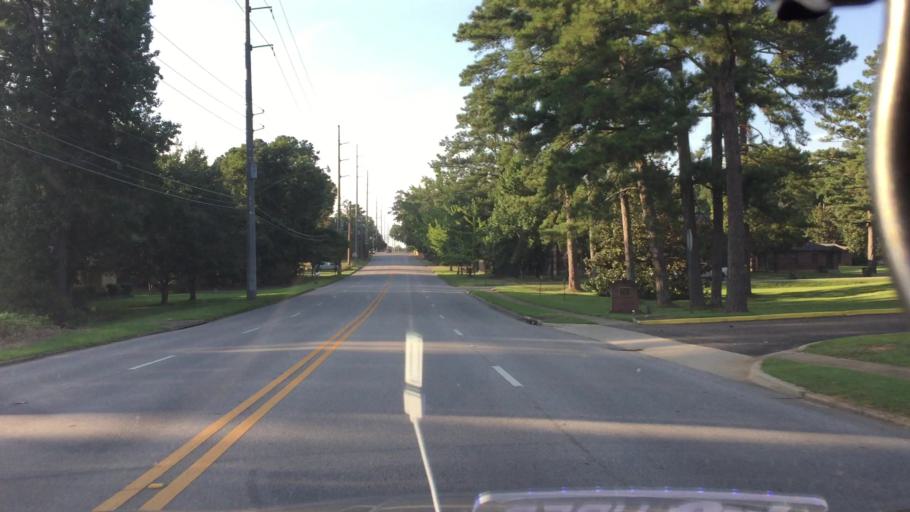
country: US
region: Alabama
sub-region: Lee County
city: Auburn
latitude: 32.6015
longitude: -85.4648
